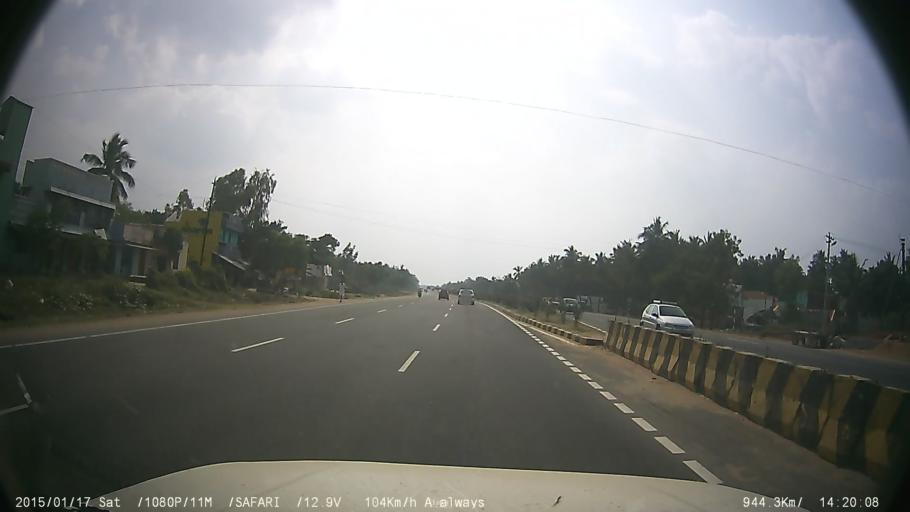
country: IN
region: Tamil Nadu
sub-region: Vellore
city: Vaniyambadi
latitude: 12.7126
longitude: 78.6546
